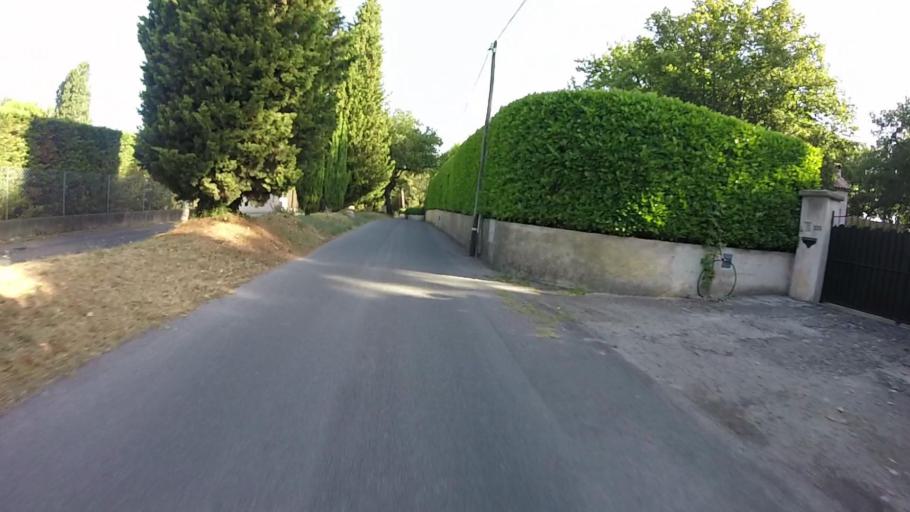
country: FR
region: Provence-Alpes-Cote d'Azur
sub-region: Departement des Alpes-Maritimes
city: Chateauneuf-Grasse
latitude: 43.6558
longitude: 6.9847
